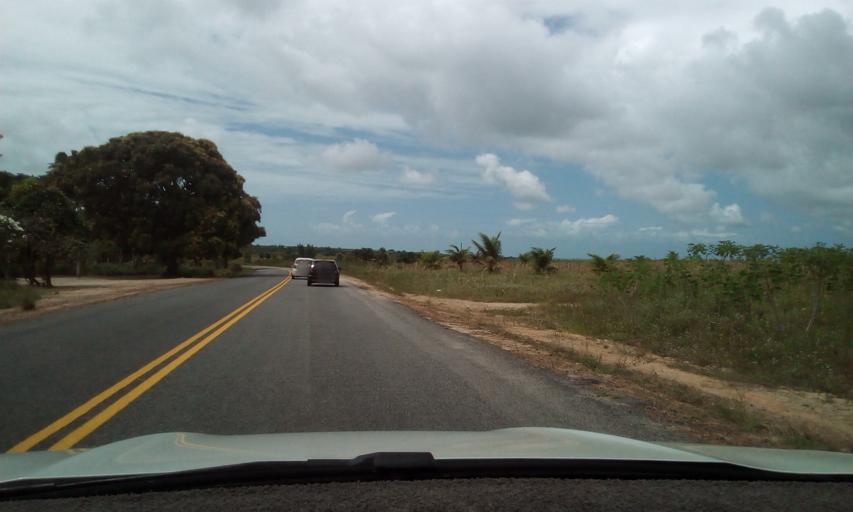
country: BR
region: Paraiba
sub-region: Rio Tinto
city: Rio Tinto
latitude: -6.7717
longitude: -35.0306
